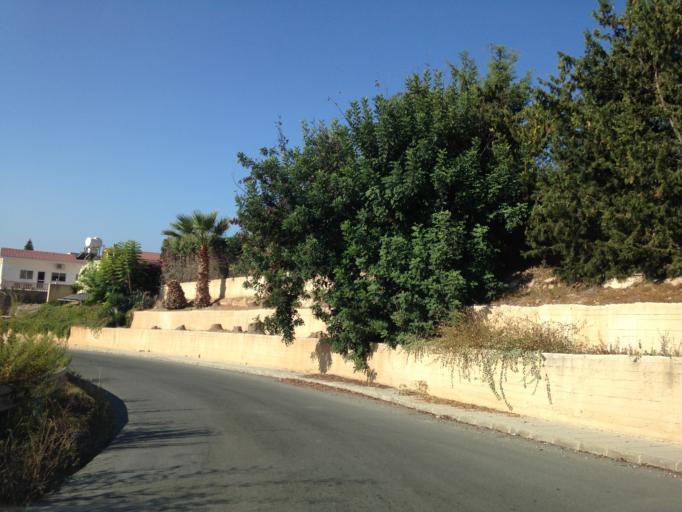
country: CY
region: Pafos
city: Pegeia
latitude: 34.8855
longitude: 32.3857
